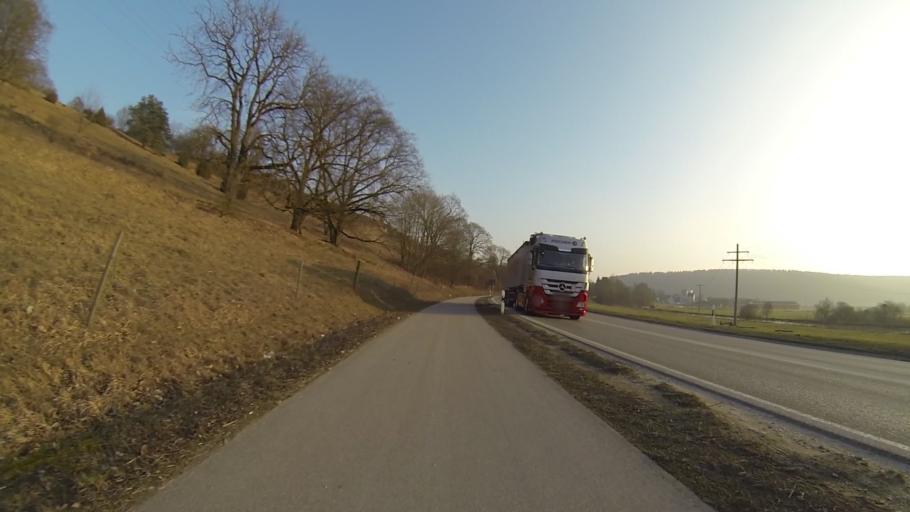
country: DE
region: Baden-Wuerttemberg
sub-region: Regierungsbezirk Stuttgart
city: Heidenheim an der Brenz
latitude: 48.7263
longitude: 10.1576
